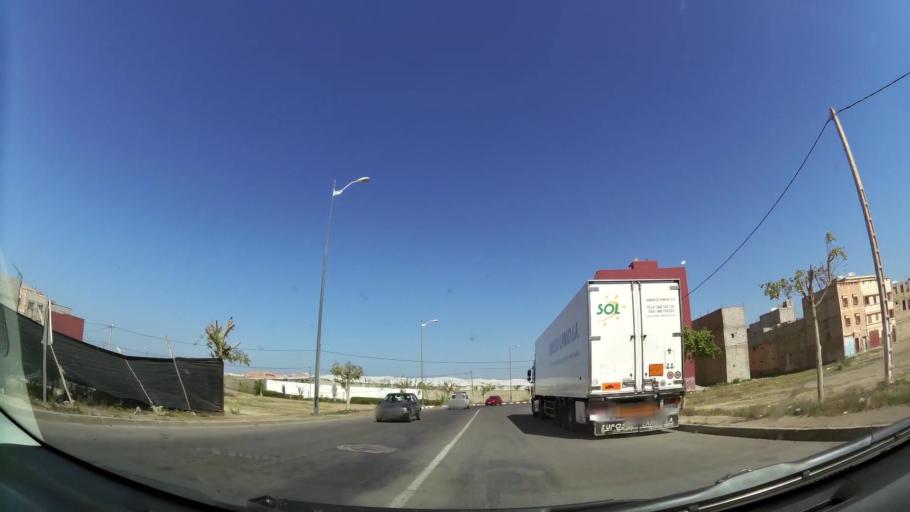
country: MA
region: Souss-Massa-Draa
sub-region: Inezgane-Ait Mellou
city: Inezgane
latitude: 30.3410
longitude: -9.5078
